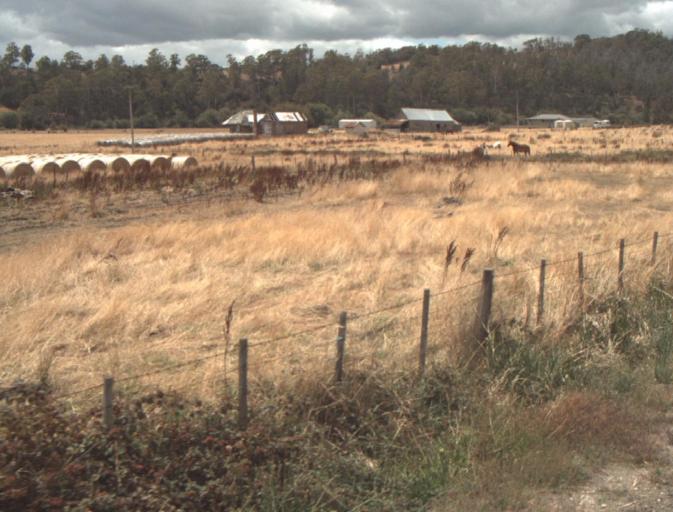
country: AU
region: Tasmania
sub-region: Launceston
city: Mayfield
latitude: -41.2263
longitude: 147.1402
